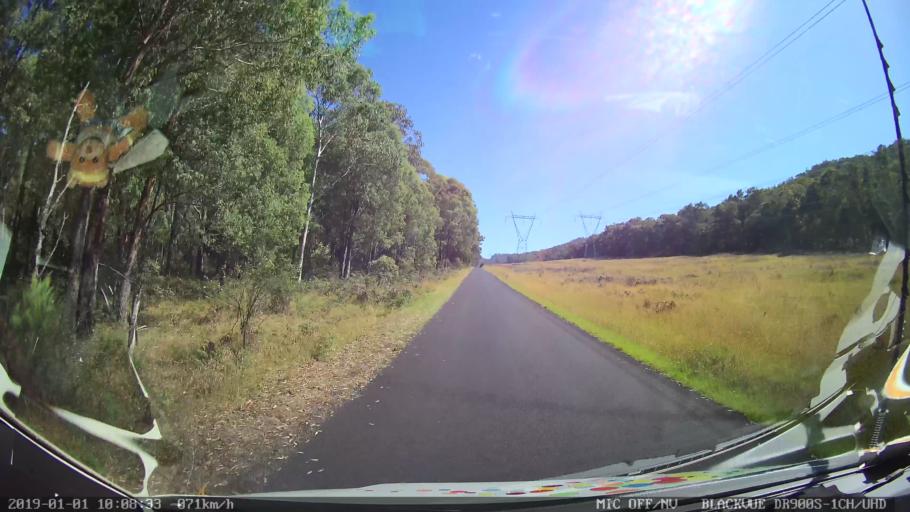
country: AU
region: New South Wales
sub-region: Snowy River
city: Jindabyne
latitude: -36.1582
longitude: 148.1576
